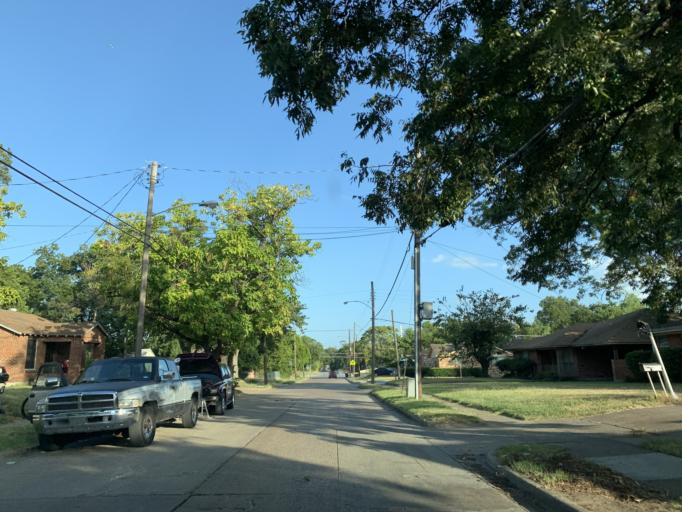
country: US
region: Texas
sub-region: Dallas County
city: Dallas
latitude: 32.7536
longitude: -96.7586
